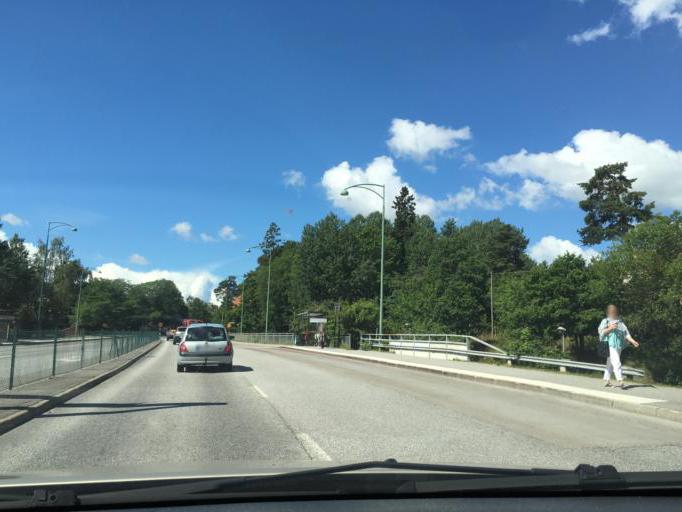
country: SE
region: Stockholm
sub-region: Nacka Kommun
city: Nacka
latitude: 59.3092
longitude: 18.1766
